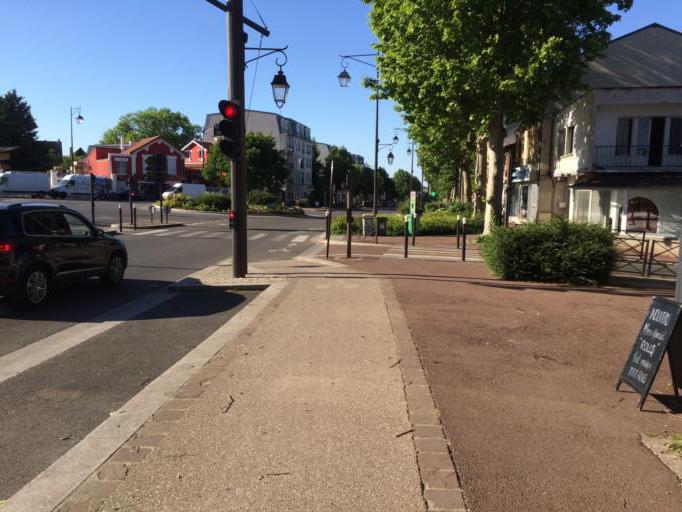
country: FR
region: Ile-de-France
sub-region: Departement des Hauts-de-Seine
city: Antony
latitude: 48.7400
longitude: 2.3024
